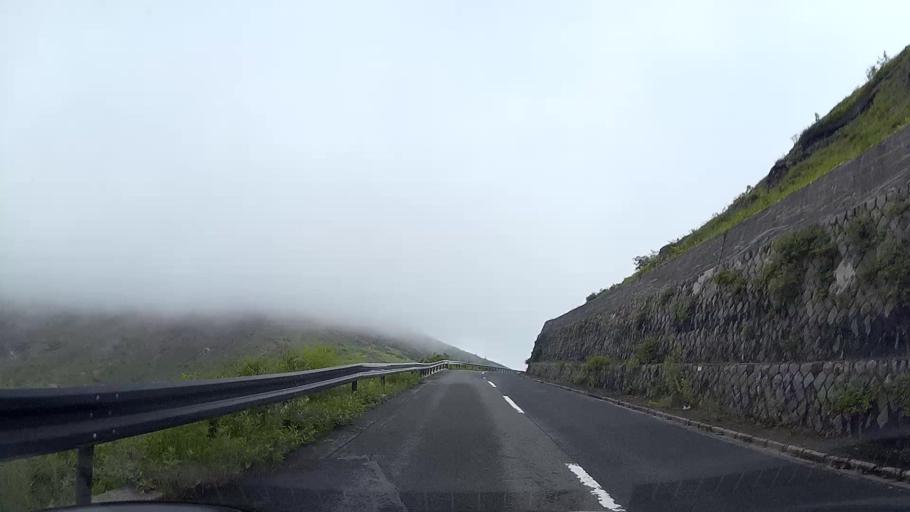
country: JP
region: Nagano
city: Nakano
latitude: 36.6503
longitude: 138.5254
